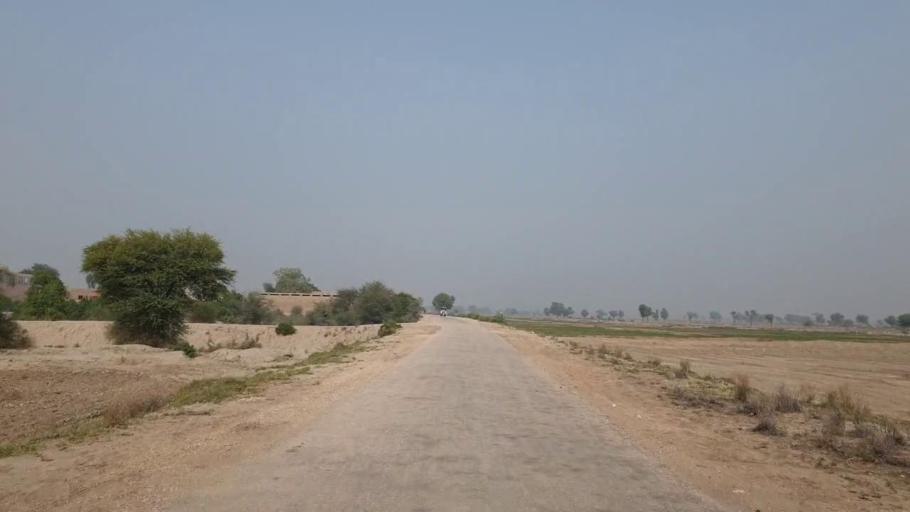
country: PK
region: Sindh
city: Bhan
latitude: 26.5134
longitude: 67.6896
